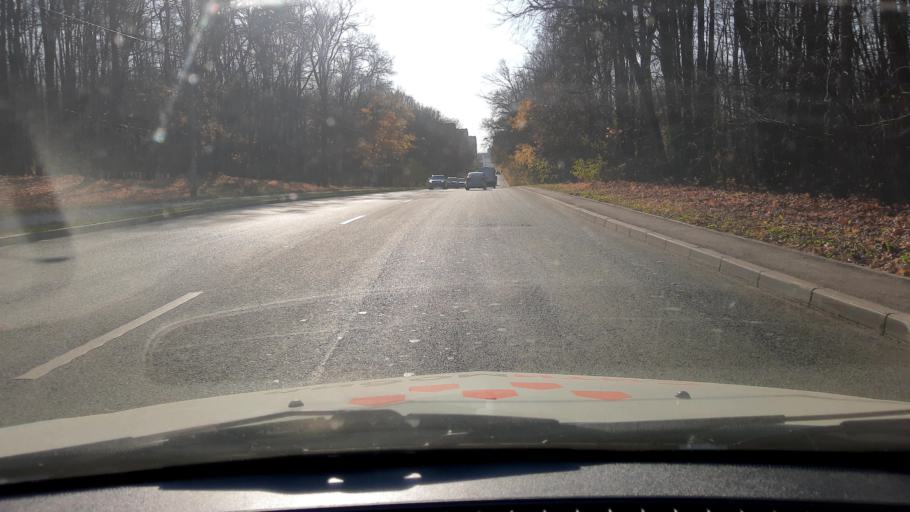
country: RU
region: Bashkortostan
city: Ufa
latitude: 54.7847
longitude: 56.0281
